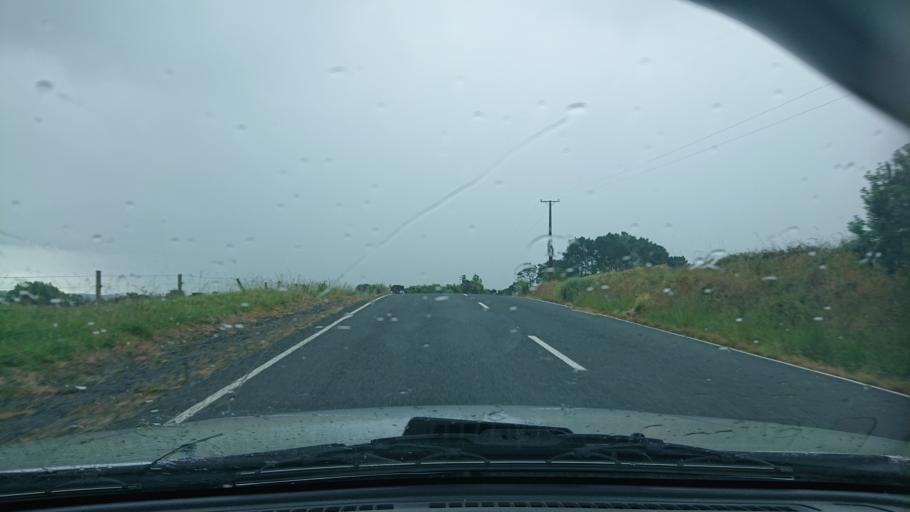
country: NZ
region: Auckland
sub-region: Auckland
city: Wellsford
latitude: -36.3334
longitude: 174.3943
